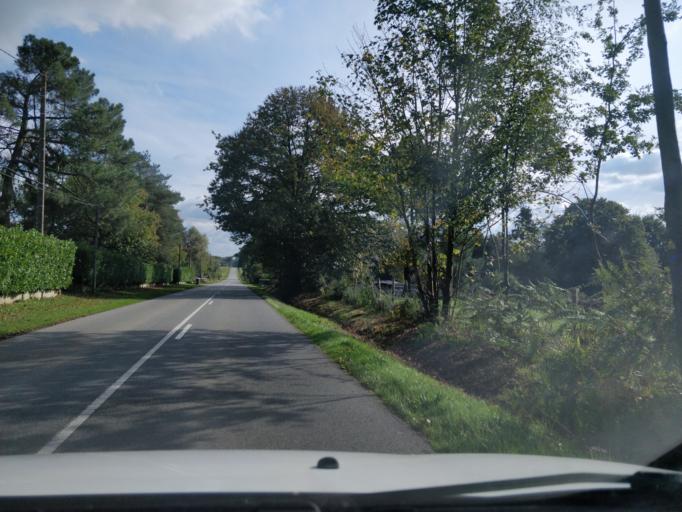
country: FR
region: Brittany
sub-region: Departement d'Ille-et-Vilaine
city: La Bouexiere
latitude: 48.1646
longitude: -1.4218
